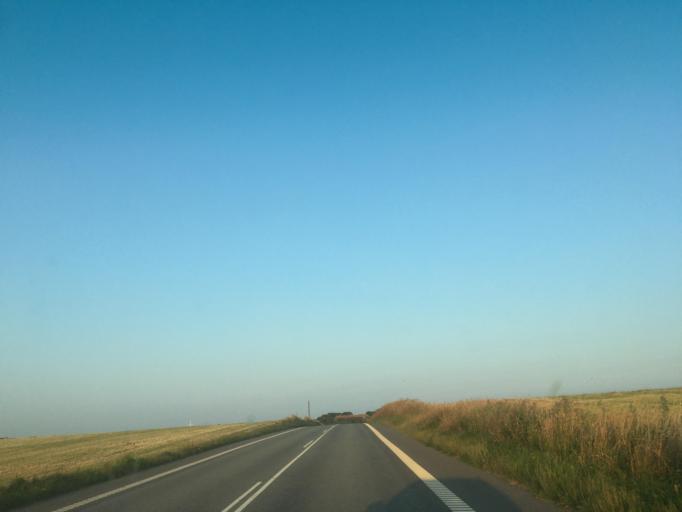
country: DK
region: Central Jutland
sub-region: Lemvig Kommune
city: Thyboron
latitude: 56.7659
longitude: 8.2987
